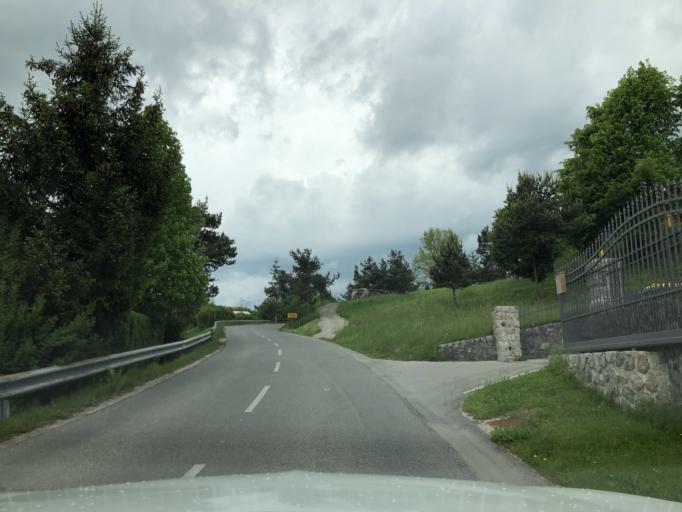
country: SI
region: Cerknica
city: Rakek
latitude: 45.8168
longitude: 14.2906
